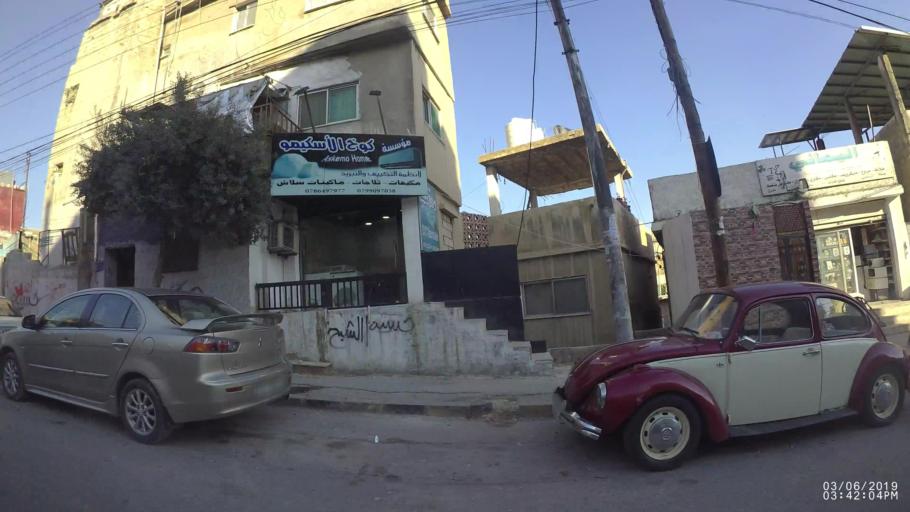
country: JO
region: Amman
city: Amman
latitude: 31.9642
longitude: 35.9592
